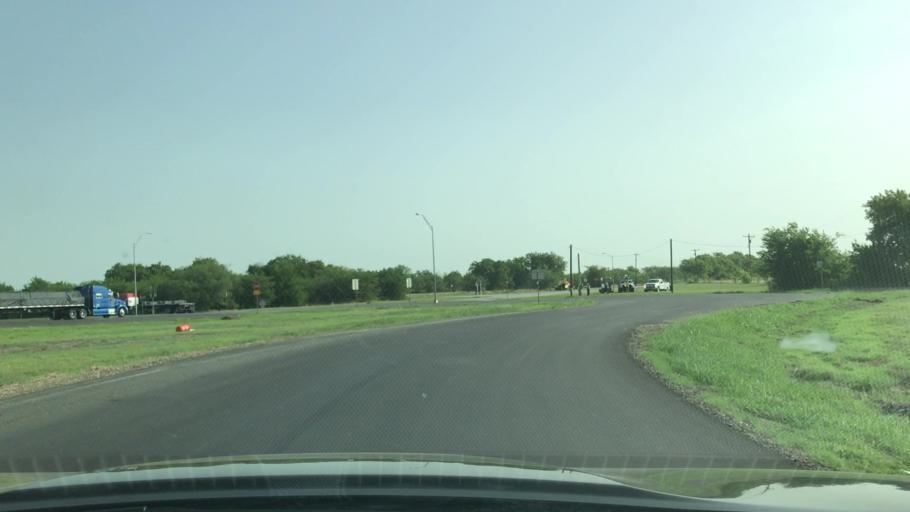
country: US
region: Texas
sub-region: Kaufman County
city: Terrell
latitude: 32.6934
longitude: -96.2401
